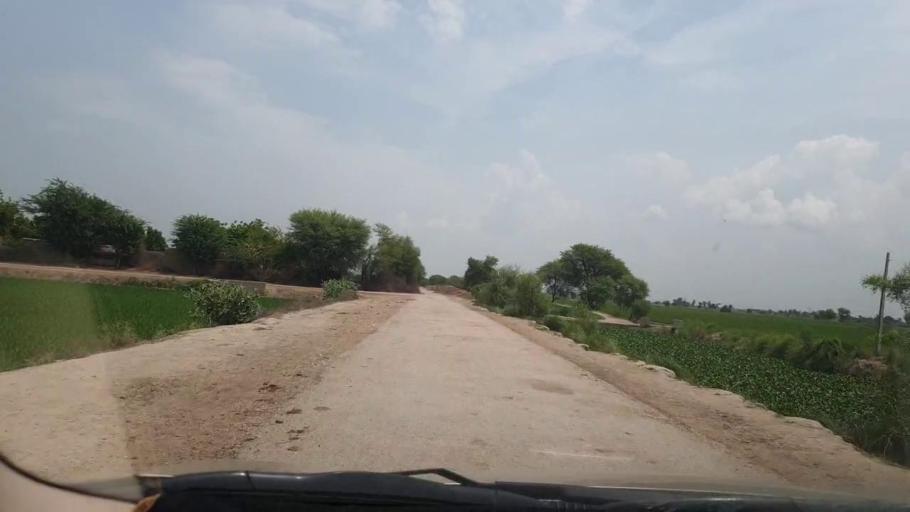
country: PK
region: Sindh
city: Larkana
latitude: 27.6086
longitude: 68.1493
